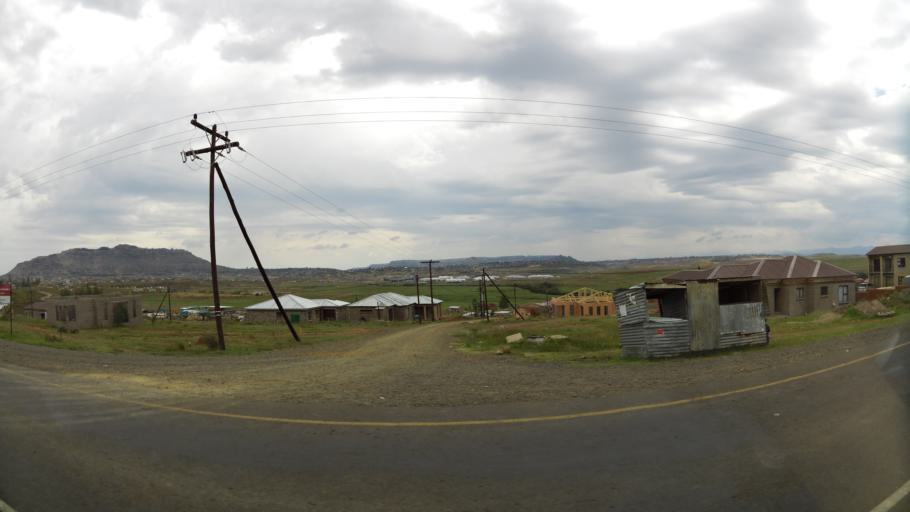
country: LS
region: Maseru
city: Maseru
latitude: -29.3910
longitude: 27.4721
